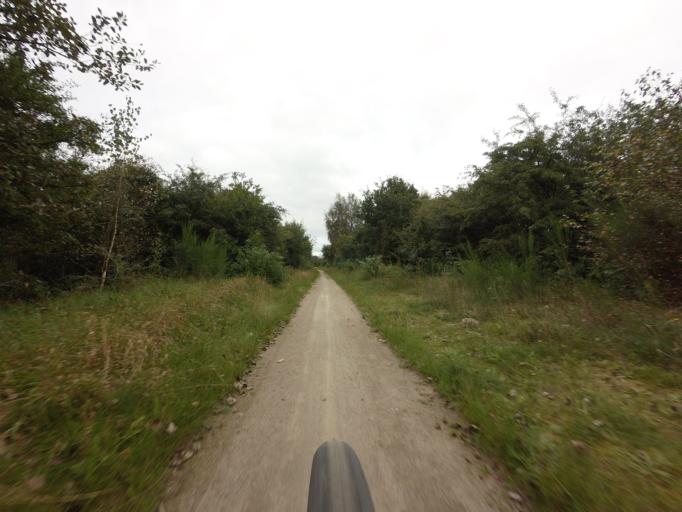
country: DK
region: South Denmark
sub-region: Billund Kommune
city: Grindsted
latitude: 55.8040
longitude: 9.0162
